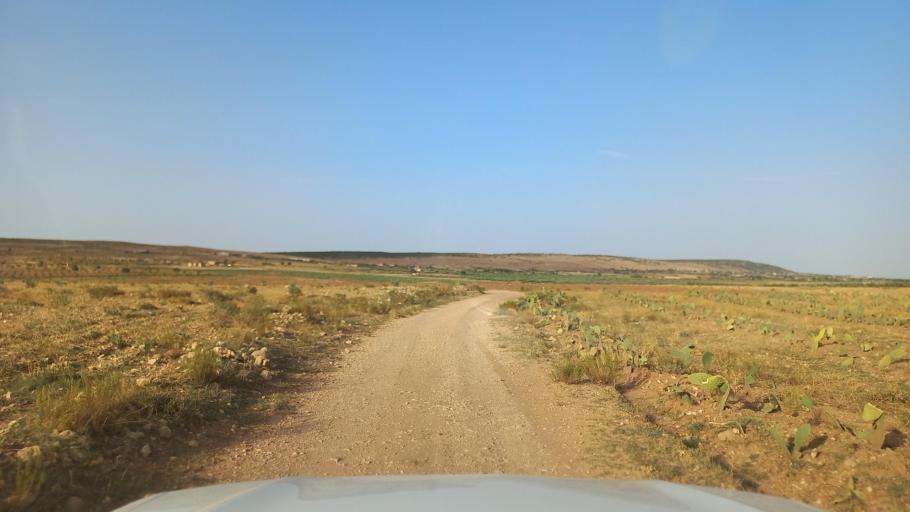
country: TN
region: Al Qasrayn
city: Kasserine
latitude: 35.3538
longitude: 8.8420
